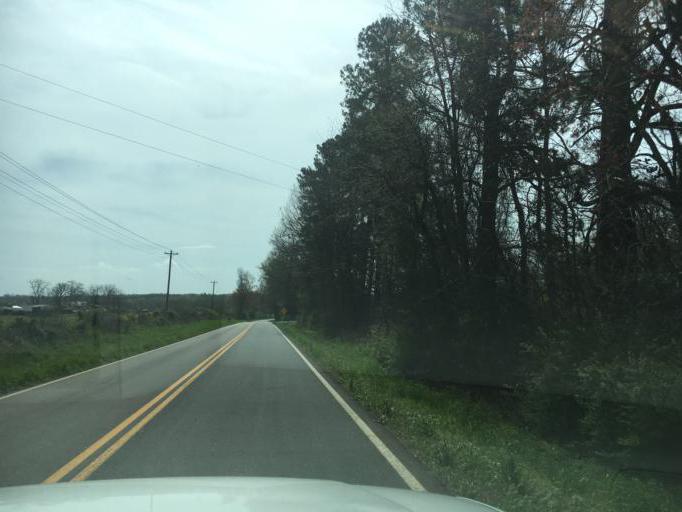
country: US
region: Georgia
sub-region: Franklin County
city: Lavonia
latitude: 34.3974
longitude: -83.0682
